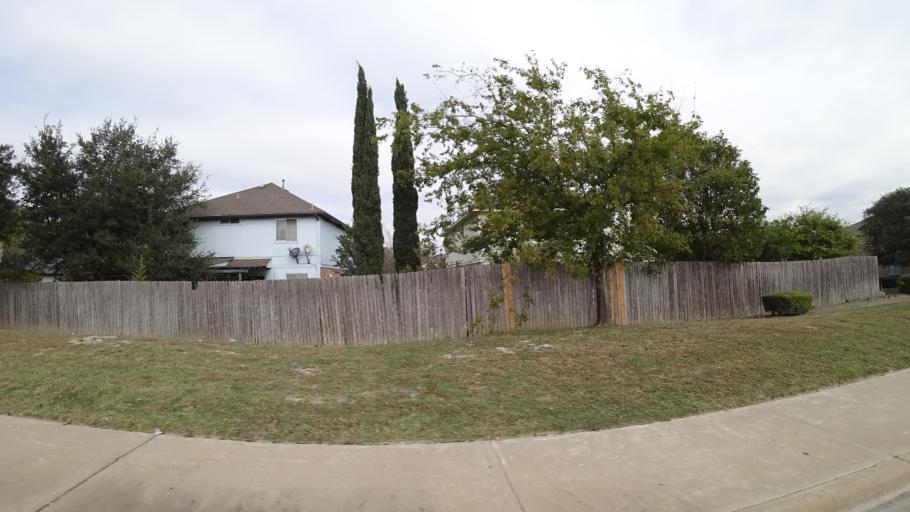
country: US
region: Texas
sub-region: Travis County
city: Windemere
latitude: 30.4563
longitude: -97.6538
